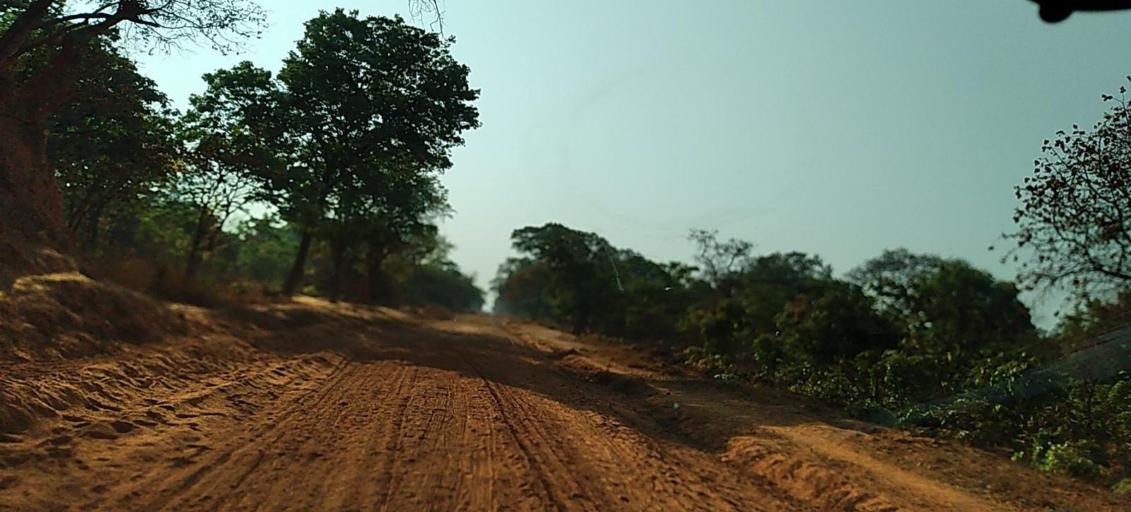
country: ZM
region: North-Western
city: Kasempa
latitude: -13.5190
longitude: 25.9508
